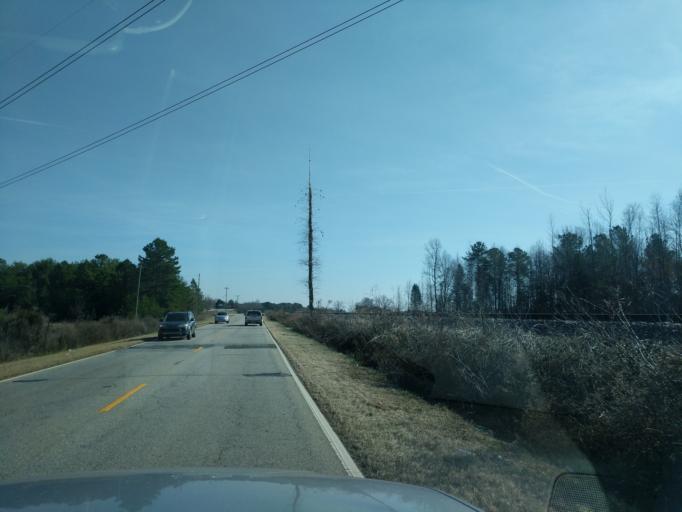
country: US
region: South Carolina
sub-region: Spartanburg County
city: Woodruff
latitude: 34.6985
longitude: -82.0045
